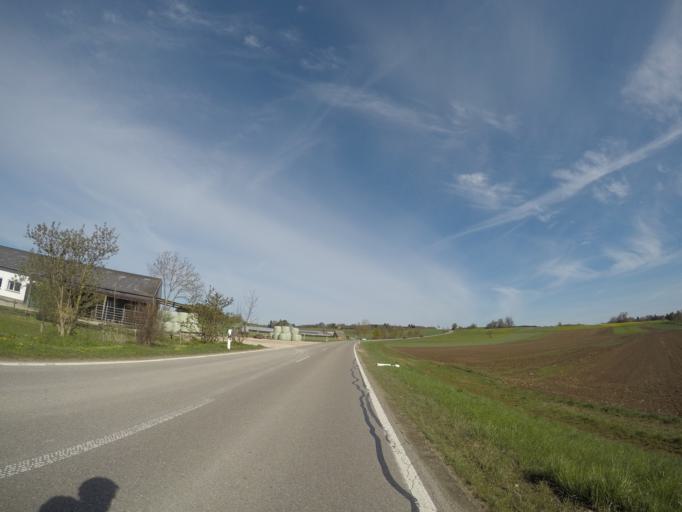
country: DE
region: Baden-Wuerttemberg
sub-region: Tuebingen Region
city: Laichingen
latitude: 48.4952
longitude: 9.6795
